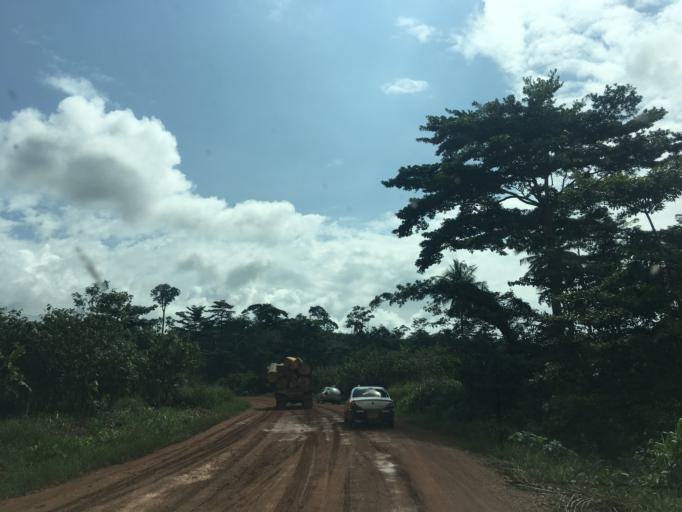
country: GH
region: Western
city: Wassa-Akropong
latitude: 5.7888
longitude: -2.3873
